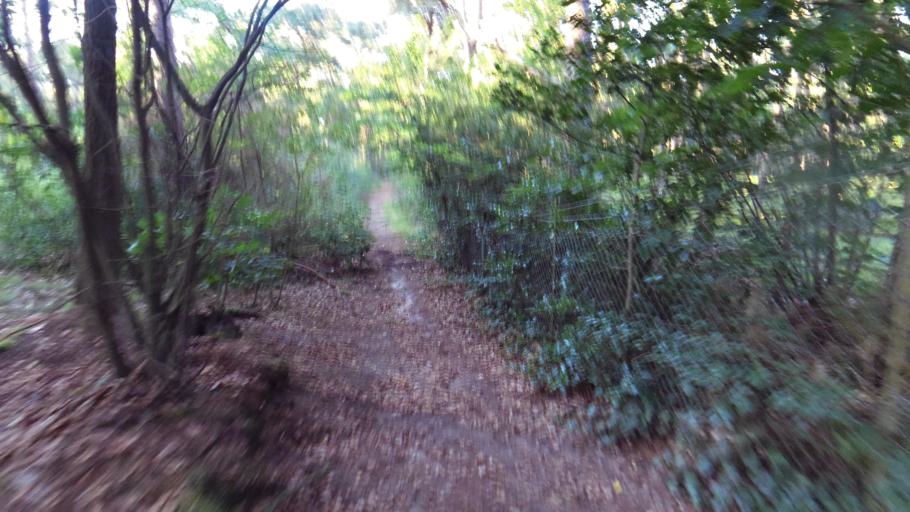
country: NL
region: Utrecht
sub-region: Gemeente Zeist
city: Zeist
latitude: 52.1267
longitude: 5.2363
